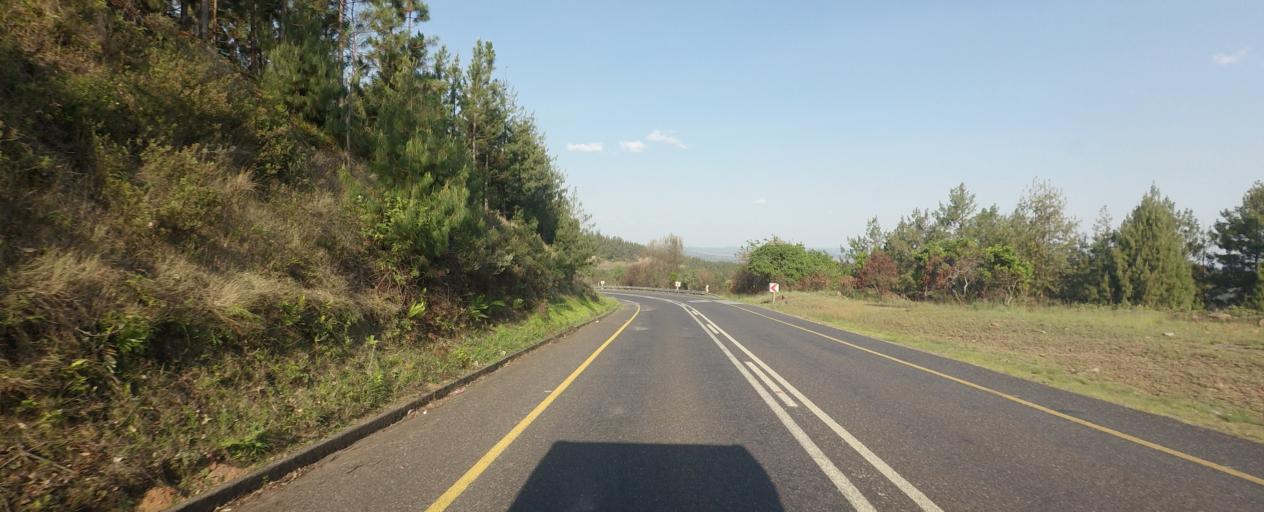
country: ZA
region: Mpumalanga
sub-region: Ehlanzeni District
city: Lydenburg
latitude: -25.1651
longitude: 30.6840
